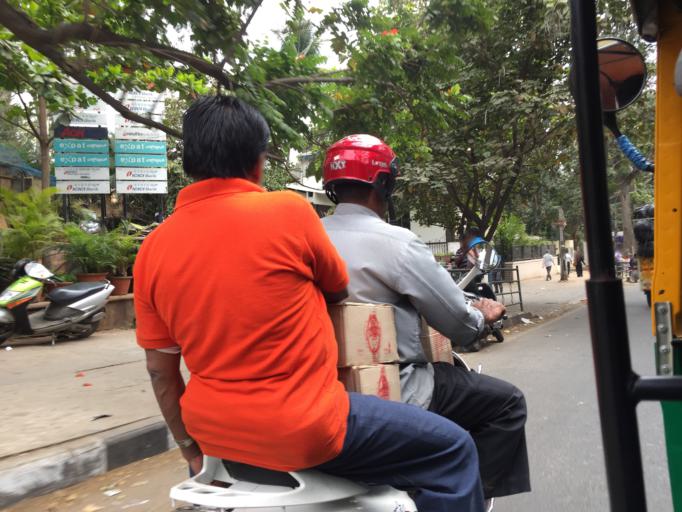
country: IN
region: Karnataka
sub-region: Bangalore Urban
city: Bangalore
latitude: 12.9731
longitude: 77.6108
